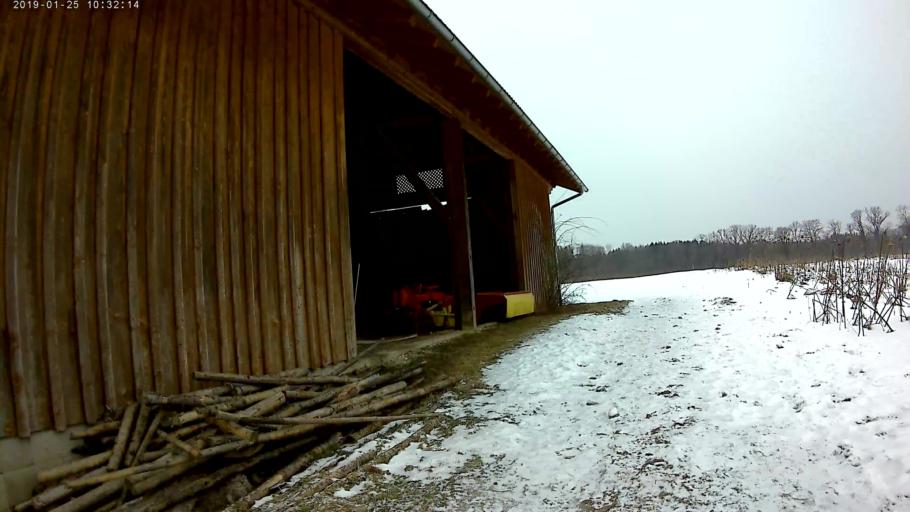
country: AT
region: Salzburg
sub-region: Politischer Bezirk Salzburg-Umgebung
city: Anif
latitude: 47.7582
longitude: 13.0547
